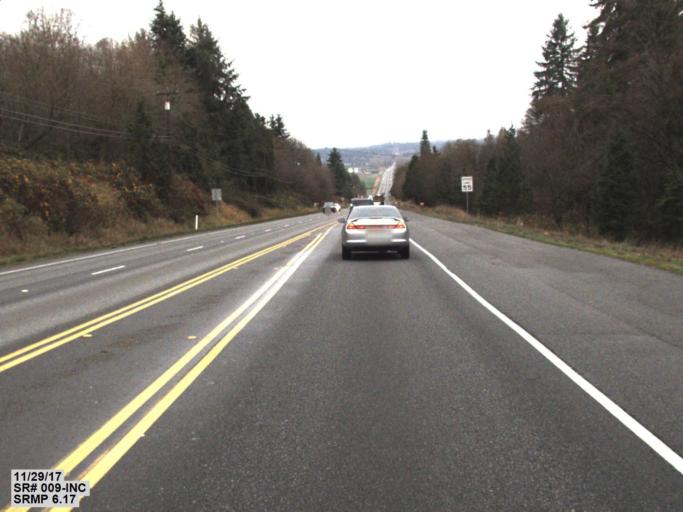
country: US
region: Washington
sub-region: Snohomish County
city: Cathcart
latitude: 47.8662
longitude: -122.1099
